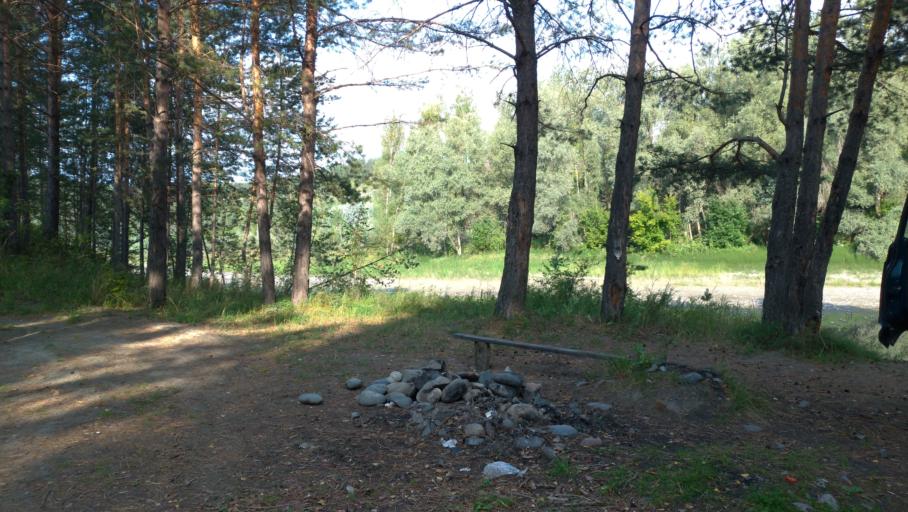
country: RU
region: Altay
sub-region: Mayminskiy Rayon
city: Manzherok
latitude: 51.8662
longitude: 85.7544
